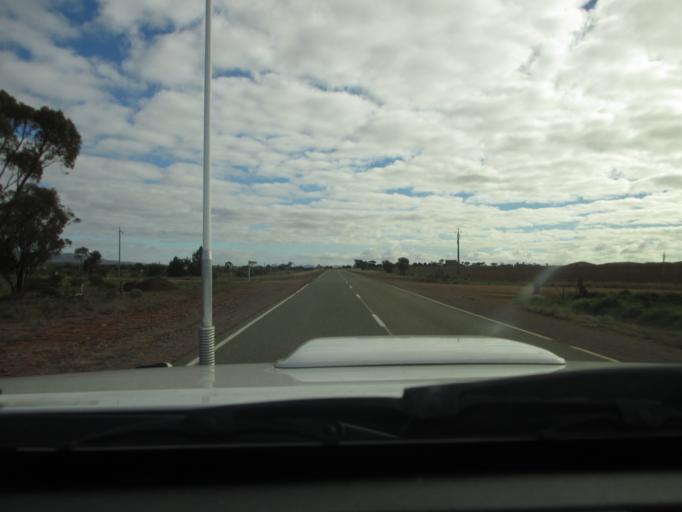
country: AU
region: South Australia
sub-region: Flinders Ranges
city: Quorn
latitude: -32.4329
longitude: 138.5328
